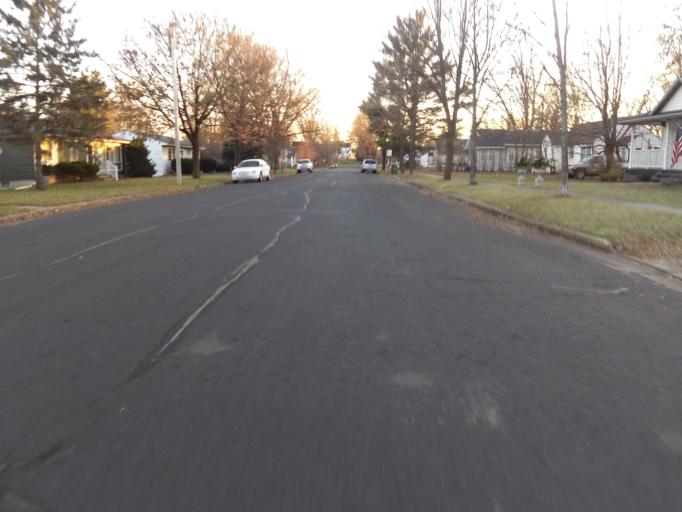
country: US
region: Wisconsin
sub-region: Pierce County
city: River Falls
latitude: 44.8604
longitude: -92.6167
